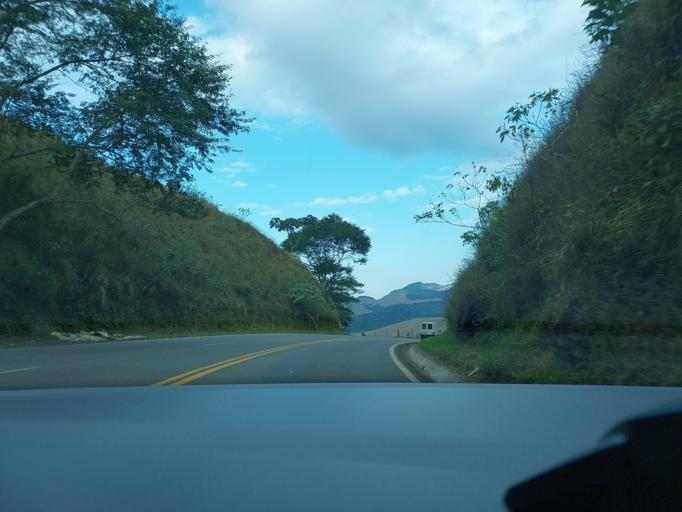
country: BR
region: Minas Gerais
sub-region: Mirai
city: Mirai
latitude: -21.0386
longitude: -42.5335
